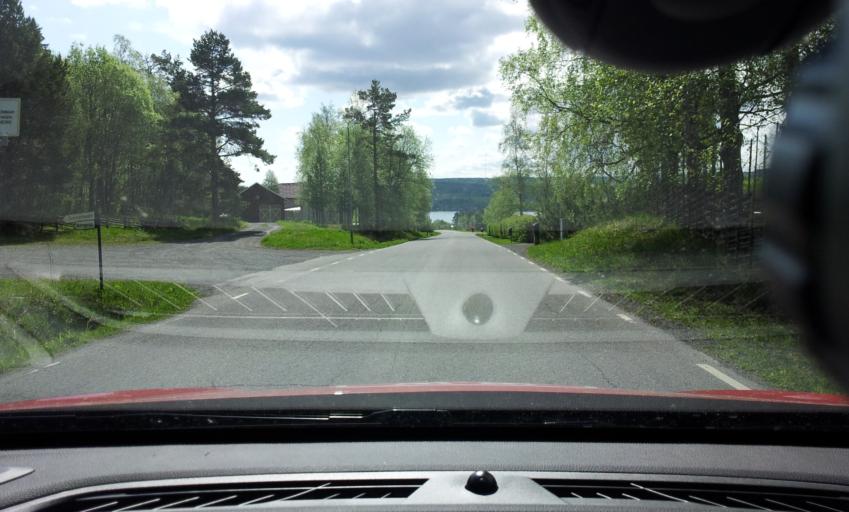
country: SE
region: Jaemtland
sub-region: OEstersunds Kommun
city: Ostersund
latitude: 63.1709
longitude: 14.5191
